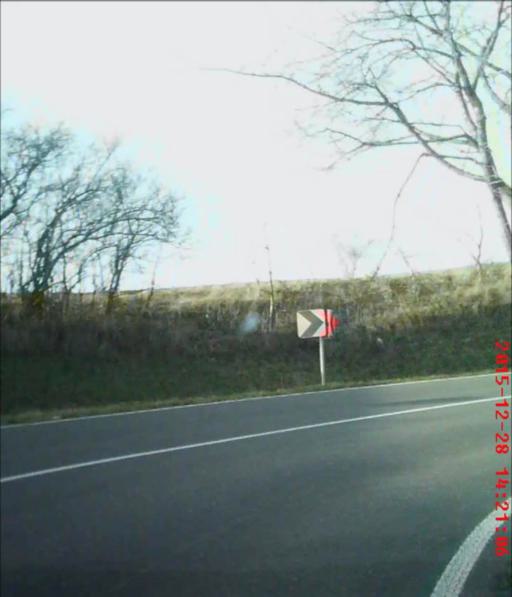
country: DE
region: Thuringia
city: Niederrossla
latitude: 51.0417
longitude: 11.4758
